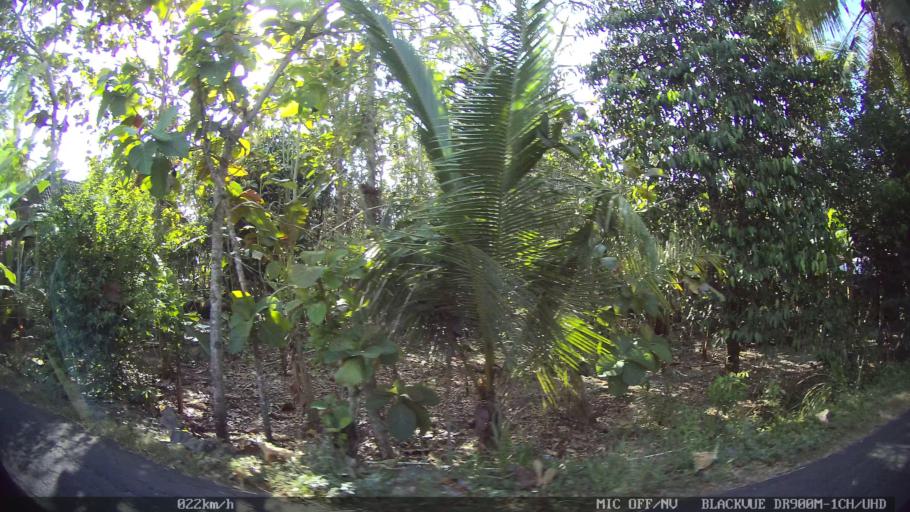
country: ID
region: Daerah Istimewa Yogyakarta
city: Kasihan
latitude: -7.8363
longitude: 110.2834
